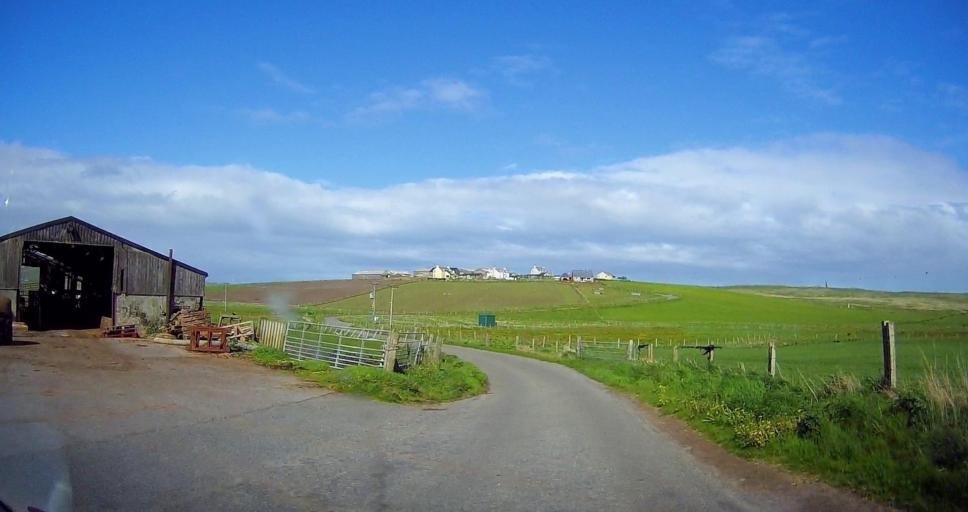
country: GB
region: Scotland
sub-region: Shetland Islands
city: Sandwick
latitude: 59.9106
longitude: -1.3329
